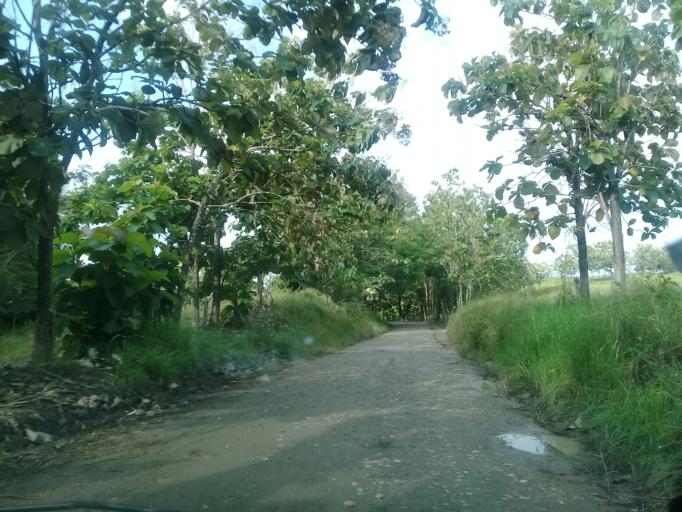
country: CO
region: Antioquia
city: Puerto Triunfo
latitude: 5.7220
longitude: -74.5338
